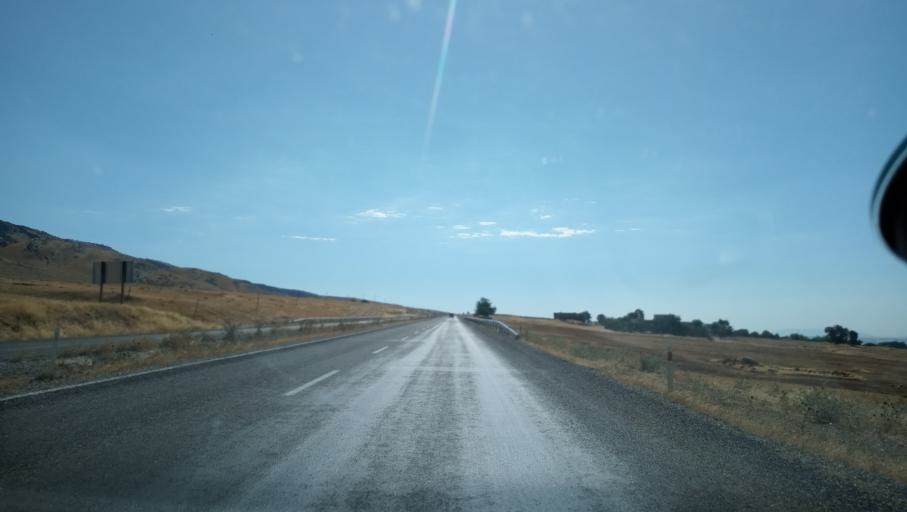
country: TR
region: Diyarbakir
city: Silvan
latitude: 38.1280
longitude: 41.0599
